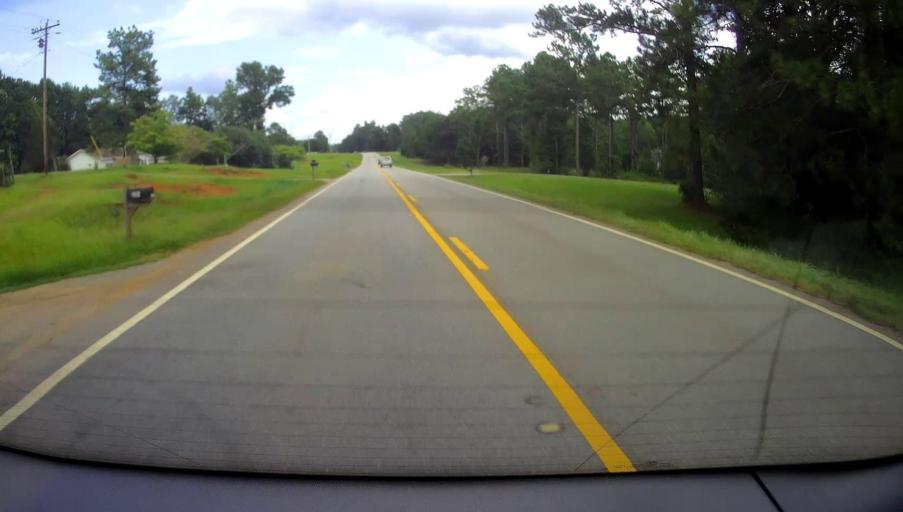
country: US
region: Georgia
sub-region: Bibb County
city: West Point
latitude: 32.8645
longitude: -83.8532
